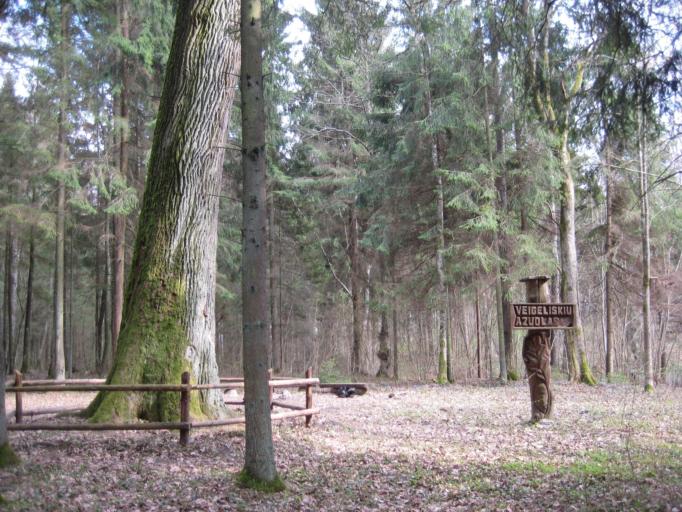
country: LT
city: Grigiskes
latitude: 54.8028
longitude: 25.0069
